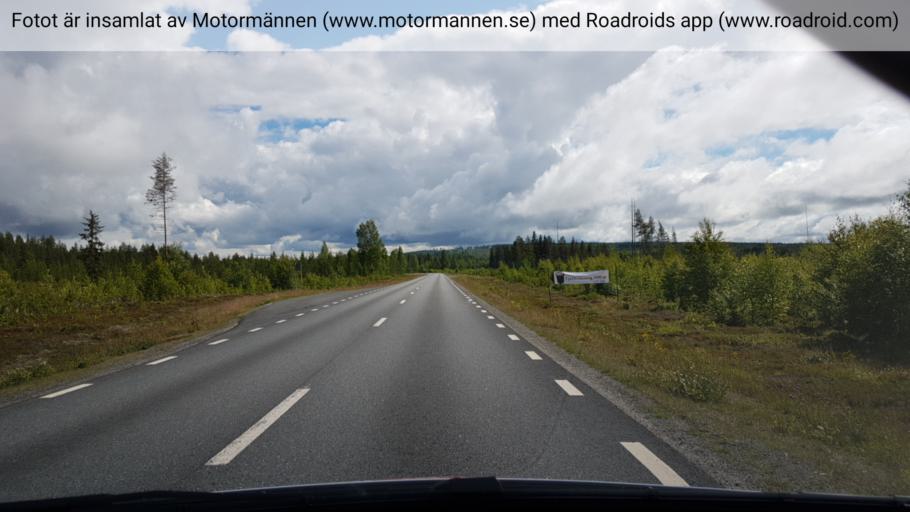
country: SE
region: Vaesterbotten
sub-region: Bjurholms Kommun
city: Bjurholm
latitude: 64.2989
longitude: 19.1755
